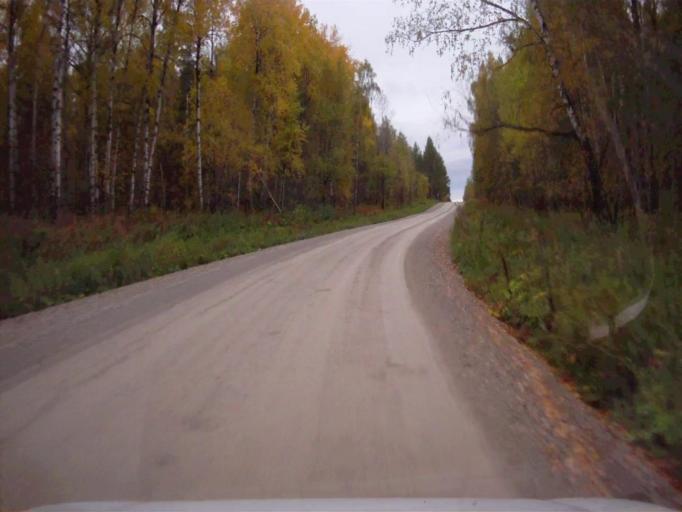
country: RU
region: Chelyabinsk
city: Nyazepetrovsk
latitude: 56.0690
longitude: 59.4325
